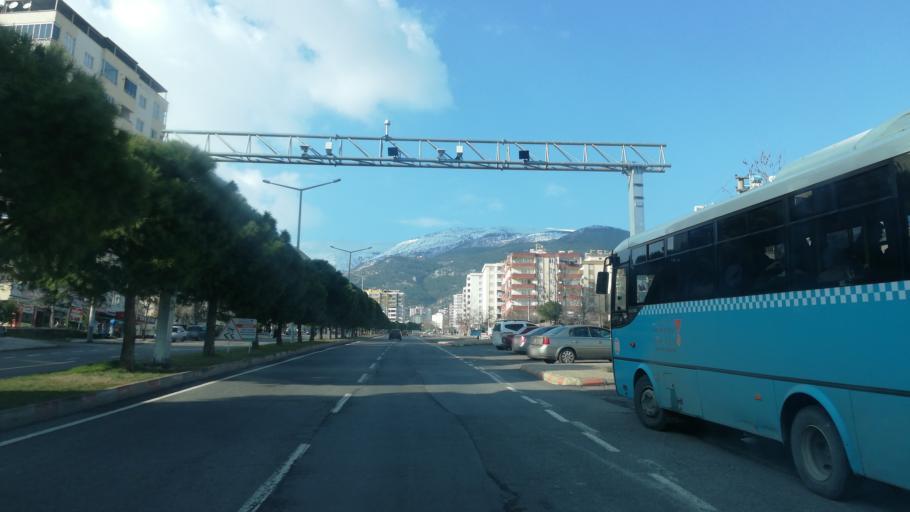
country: TR
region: Kahramanmaras
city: Kahramanmaras
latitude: 37.5933
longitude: 36.8989
